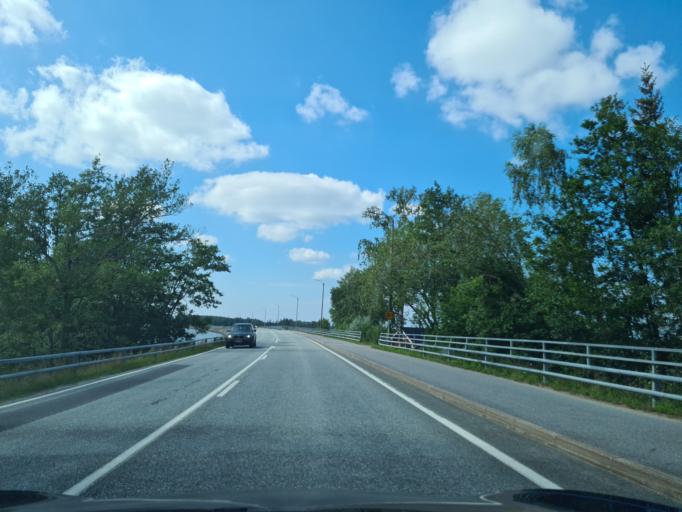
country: FI
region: Ostrobothnia
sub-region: Vaasa
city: Replot
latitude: 63.2050
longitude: 21.5201
